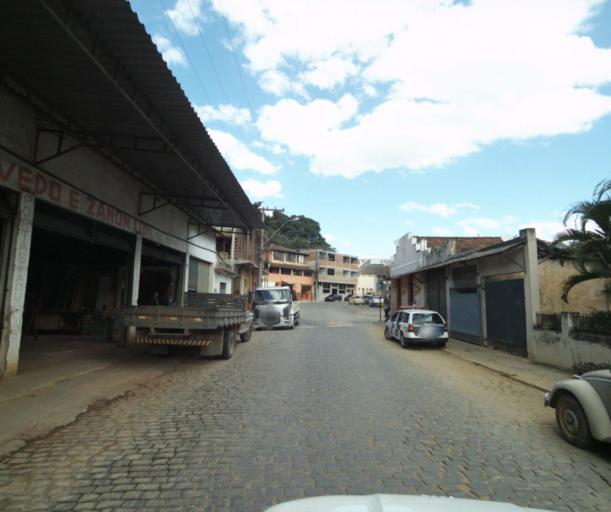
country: BR
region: Espirito Santo
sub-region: Sao Jose Do Calcado
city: Sao Jose do Calcado
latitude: -21.0287
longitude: -41.6555
